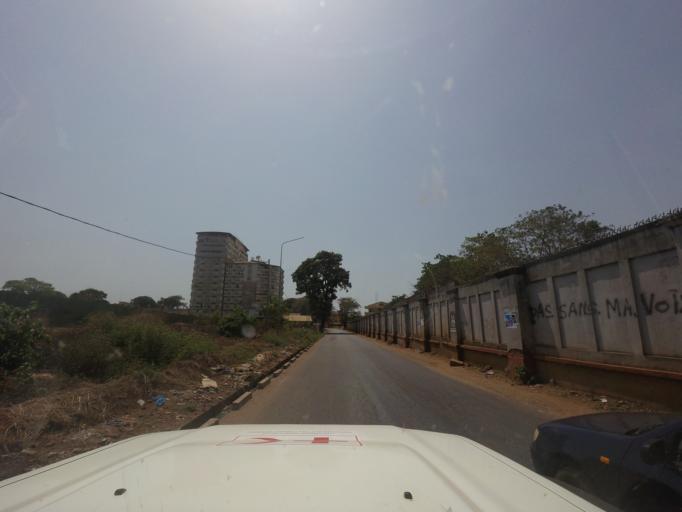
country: GN
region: Conakry
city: Camayenne
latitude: 9.5159
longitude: -13.7105
